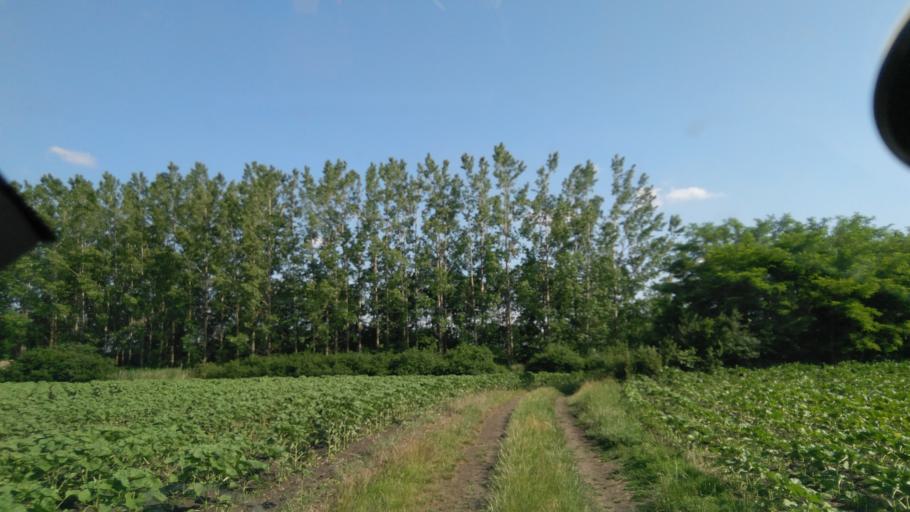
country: HU
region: Bekes
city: Doboz
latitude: 46.7010
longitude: 21.2377
